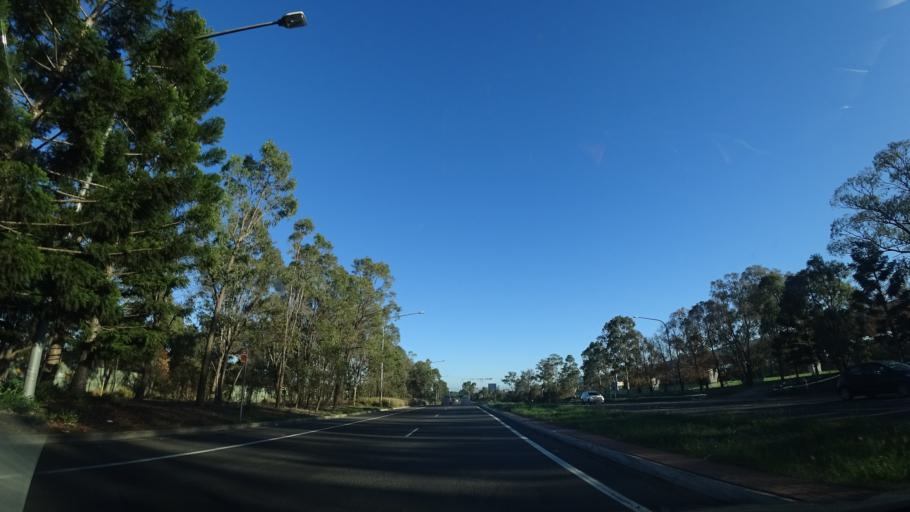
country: AU
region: New South Wales
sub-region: Blacktown
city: Stanhope Gardens
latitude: -33.7202
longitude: 150.9378
